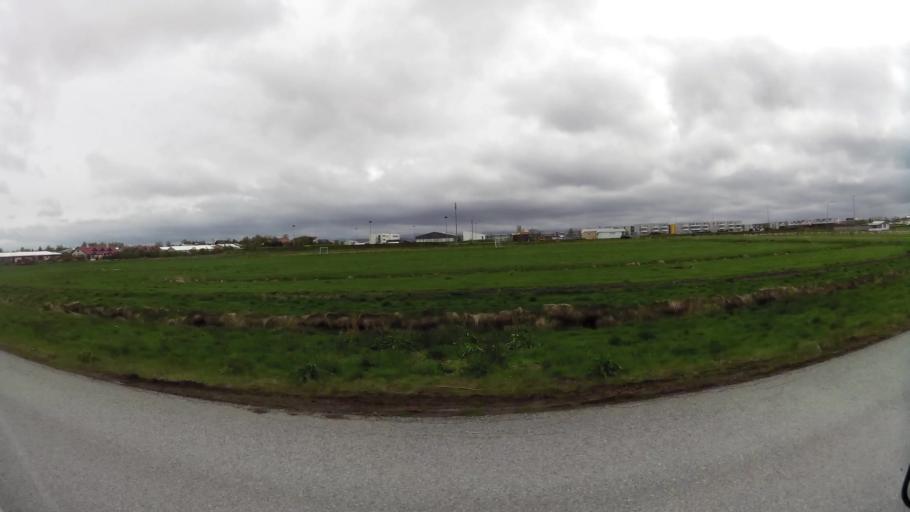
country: IS
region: Capital Region
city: Alftanes
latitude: 64.1069
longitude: -22.0248
